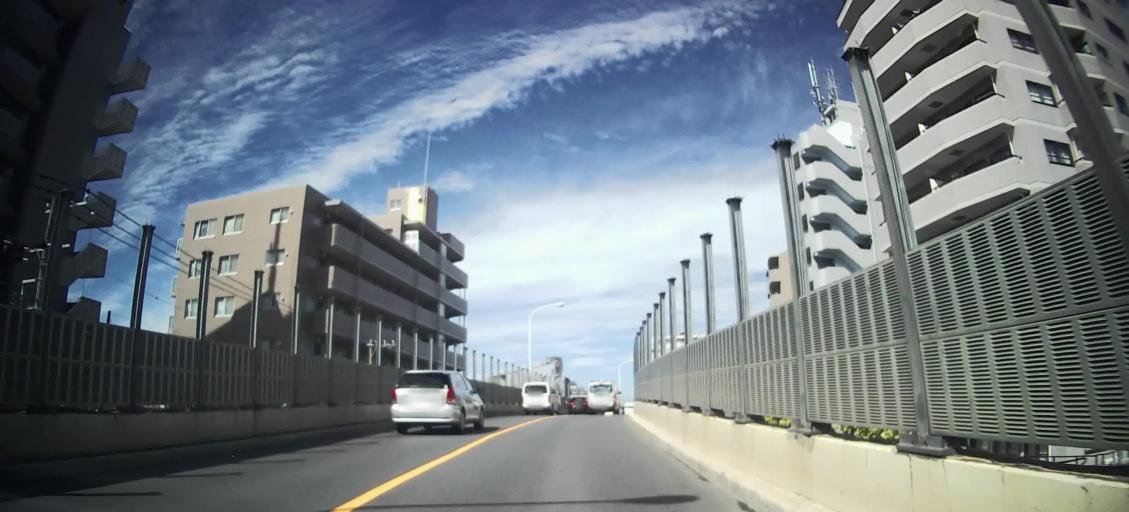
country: JP
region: Saitama
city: Wako
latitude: 35.7495
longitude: 139.6149
